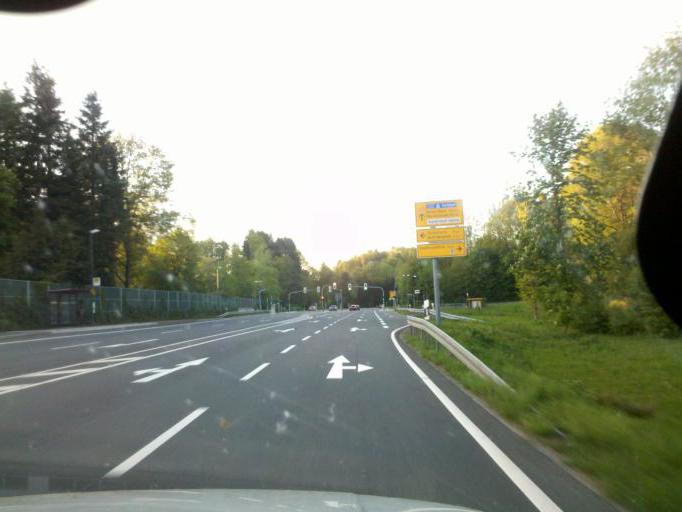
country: DE
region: North Rhine-Westphalia
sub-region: Regierungsbezirk Koln
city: Gummersbach
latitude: 51.0109
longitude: 7.5569
